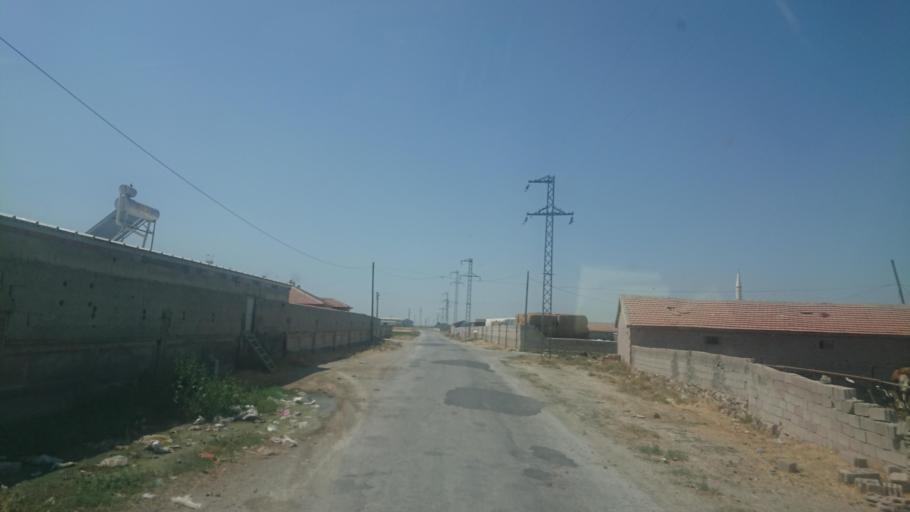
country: TR
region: Aksaray
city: Sultanhani
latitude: 38.2880
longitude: 33.7155
